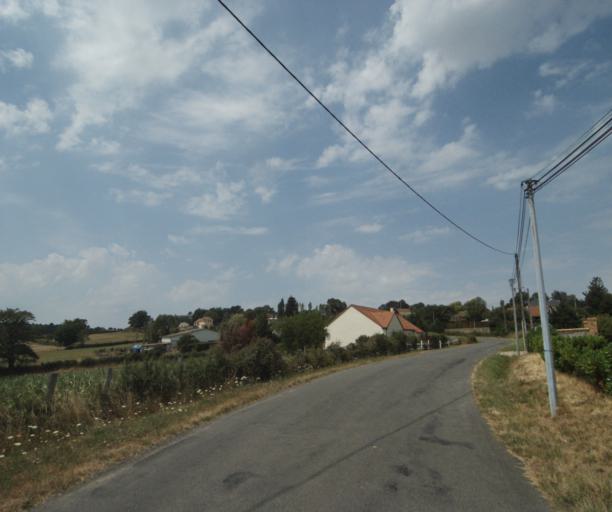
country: FR
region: Bourgogne
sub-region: Departement de Saone-et-Loire
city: Gueugnon
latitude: 46.5970
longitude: 4.0246
